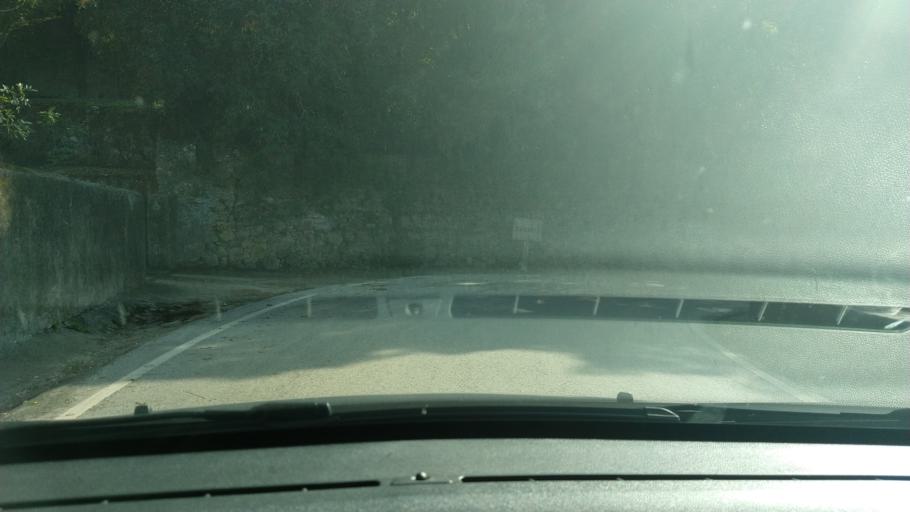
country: PT
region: Lisbon
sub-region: Sintra
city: Colares
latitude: 38.7954
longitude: -9.4313
